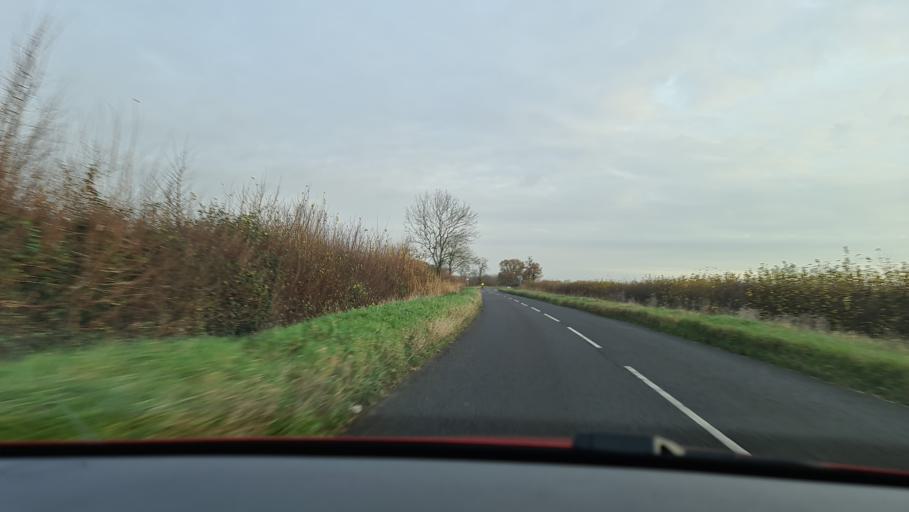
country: GB
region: England
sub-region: Oxfordshire
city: Kidlington
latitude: 51.8290
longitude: -1.2175
